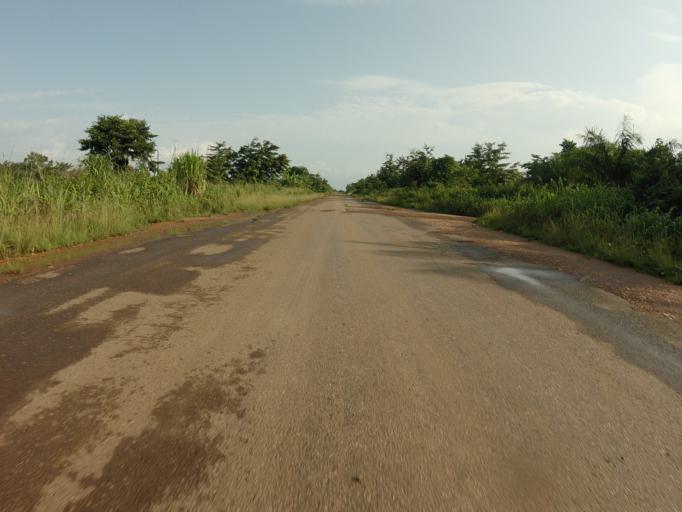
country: GH
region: Volta
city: Hohoe
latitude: 7.0697
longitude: 0.4350
